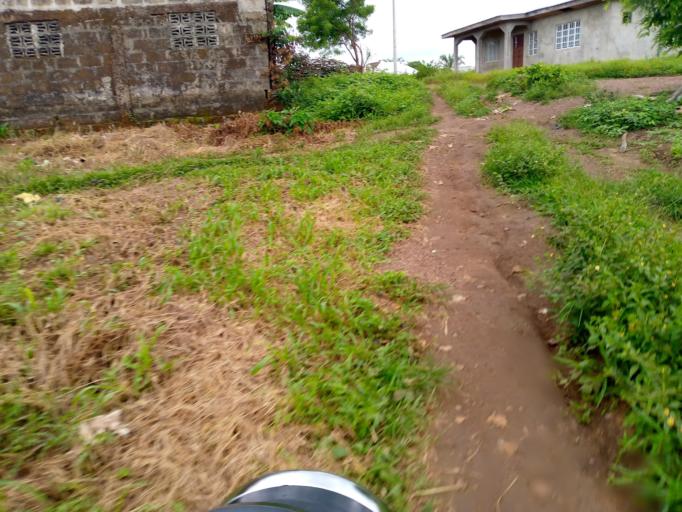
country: SL
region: Southern Province
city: Moyamba
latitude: 8.1539
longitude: -12.4370
